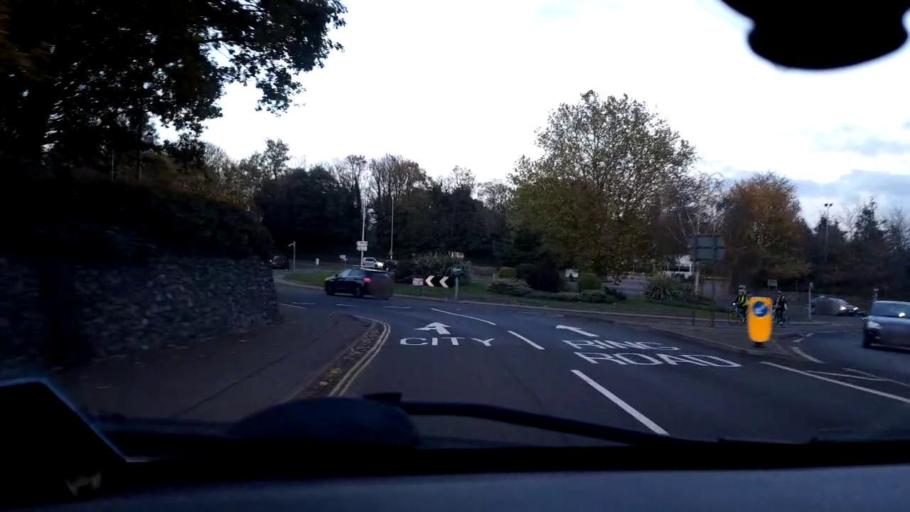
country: GB
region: England
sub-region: Norfolk
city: Thorpe Hamlet
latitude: 52.6155
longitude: 1.3098
